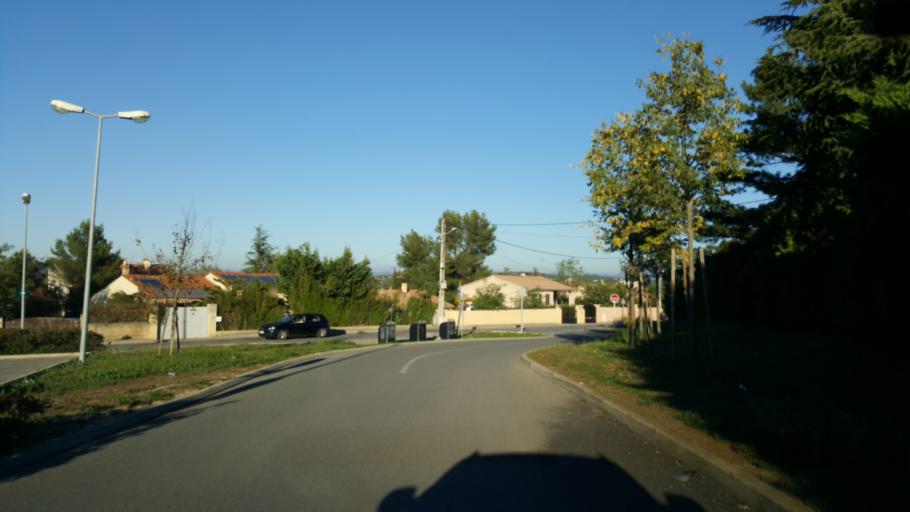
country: FR
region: Provence-Alpes-Cote d'Azur
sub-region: Departement du Var
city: Saint-Maximin-la-Sainte-Baume
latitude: 43.4501
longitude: 5.8534
